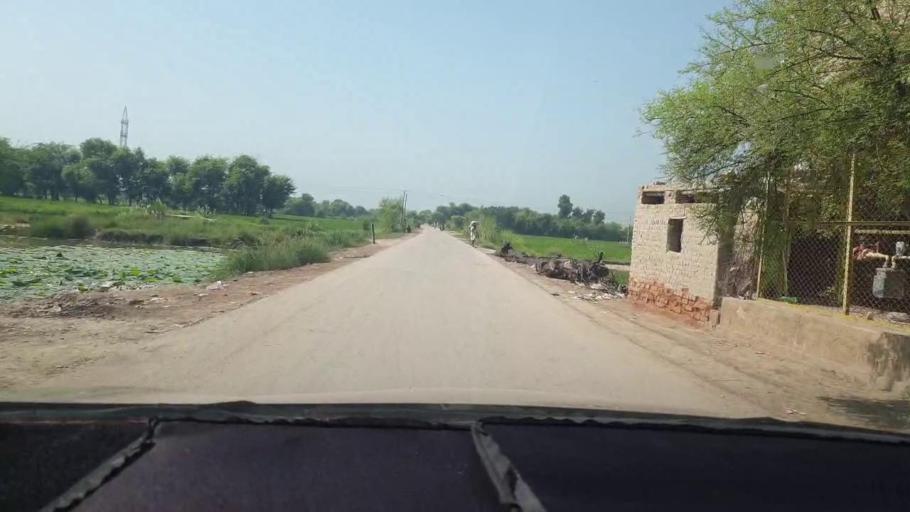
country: PK
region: Sindh
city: Kambar
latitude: 27.5869
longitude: 68.0490
